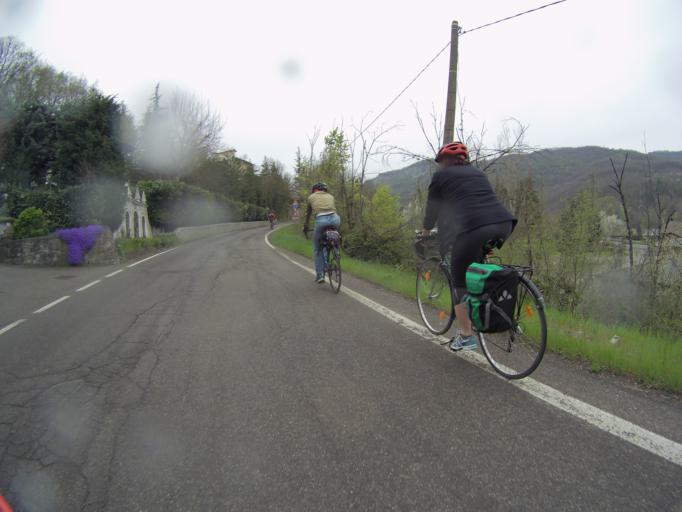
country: IT
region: Emilia-Romagna
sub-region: Provincia di Reggio Emilia
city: Ciano d'Enza
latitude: 44.5724
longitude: 10.4064
